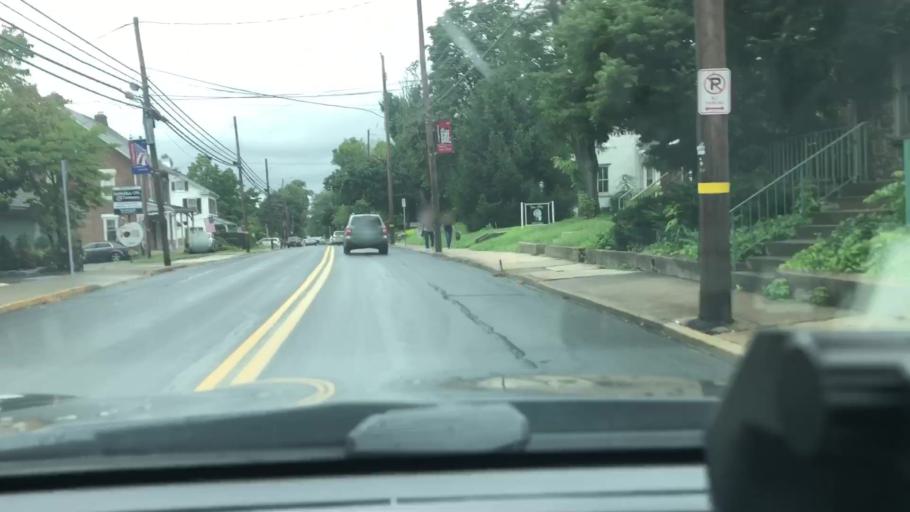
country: US
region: Pennsylvania
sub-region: Lehigh County
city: Coopersburg
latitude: 40.5134
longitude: -75.3898
